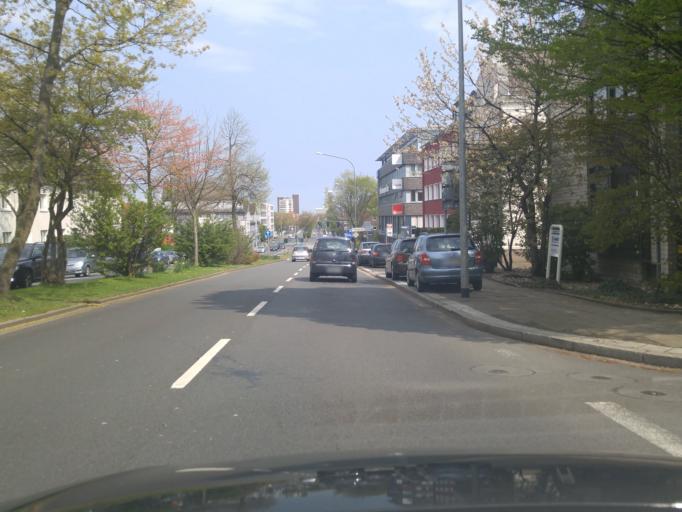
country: DE
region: North Rhine-Westphalia
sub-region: Regierungsbezirk Dusseldorf
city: Essen
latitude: 51.4209
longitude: 6.9985
